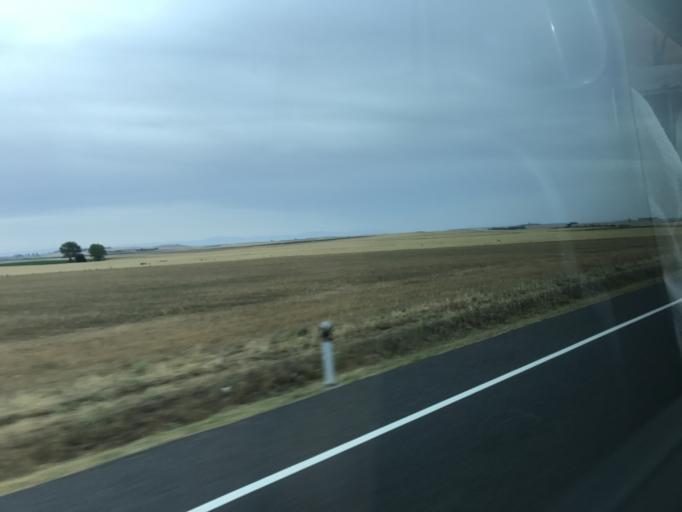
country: ES
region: Castille and Leon
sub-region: Provincia de Segovia
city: Rapariegos
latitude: 41.0851
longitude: -4.6365
